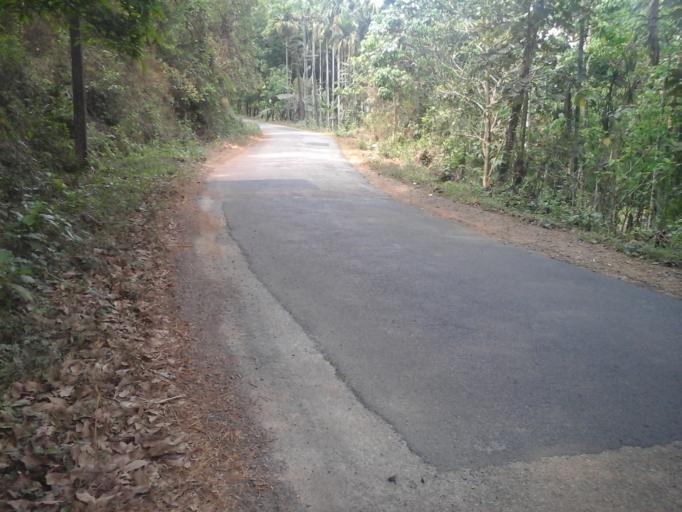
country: IN
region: Kerala
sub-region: Kannur
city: Taliparamba
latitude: 12.1484
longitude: 75.4351
